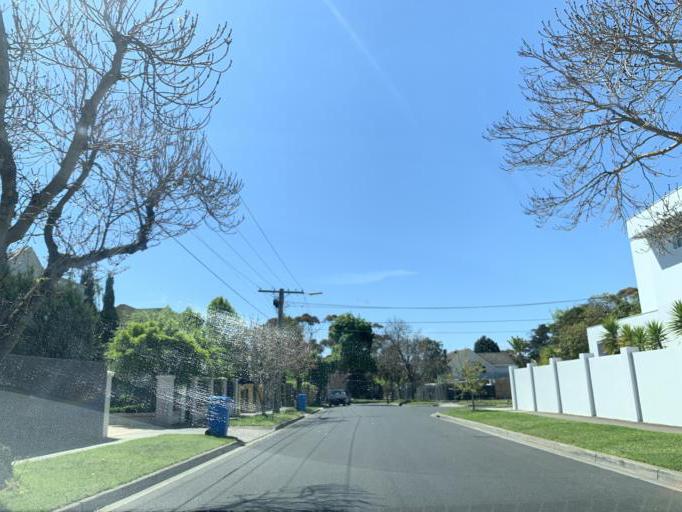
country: AU
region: Victoria
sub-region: Bayside
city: Hampton
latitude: -37.9284
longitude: 145.0137
